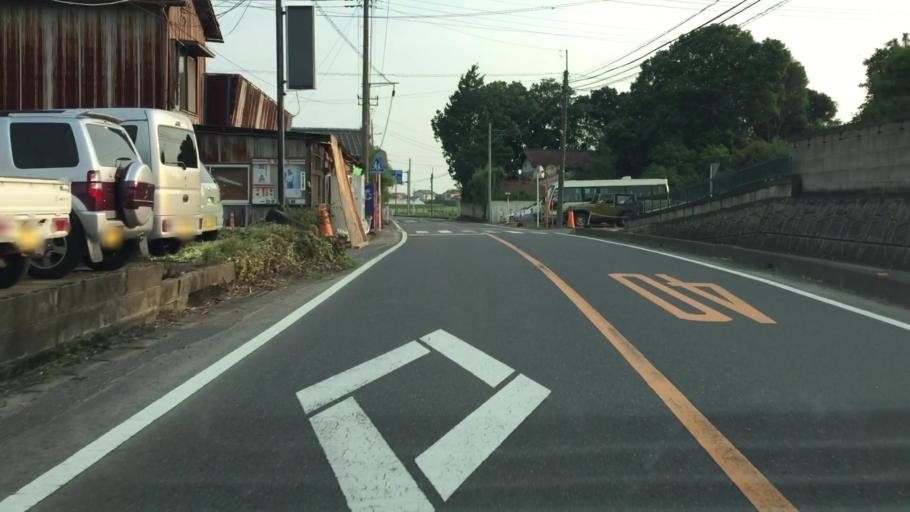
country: JP
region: Tochigi
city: Fujioka
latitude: 36.2508
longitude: 139.6193
